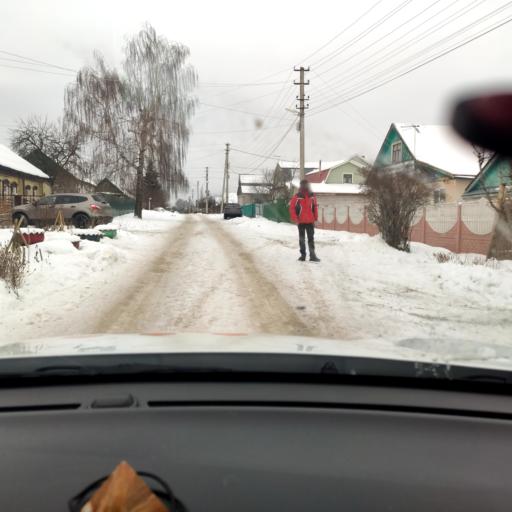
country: RU
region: Tatarstan
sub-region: Gorod Kazan'
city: Kazan
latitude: 55.8607
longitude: 49.0665
